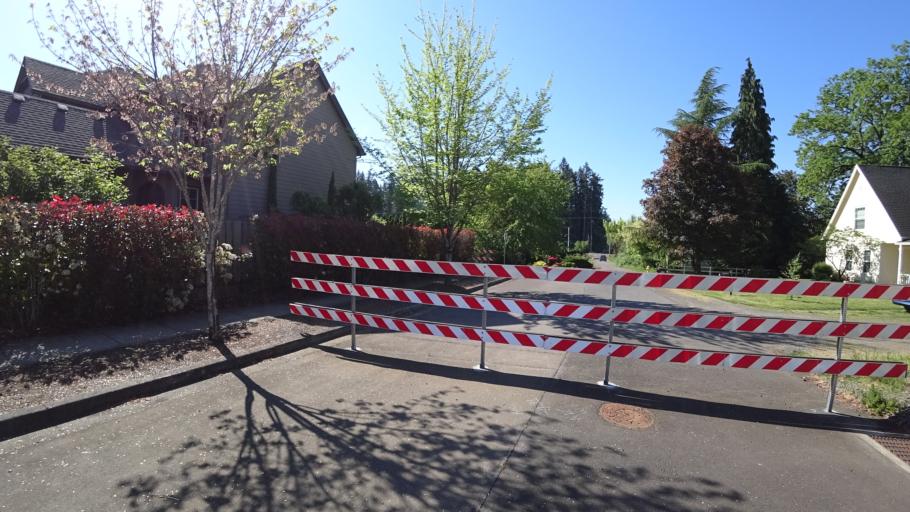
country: US
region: Oregon
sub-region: Washington County
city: Rockcreek
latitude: 45.5215
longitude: -122.9199
